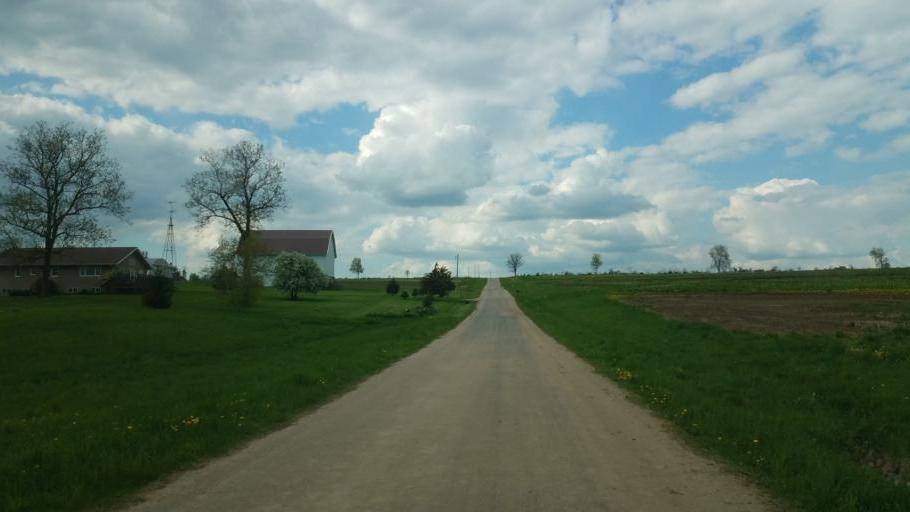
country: US
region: Wisconsin
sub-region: Vernon County
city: Hillsboro
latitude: 43.5868
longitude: -90.3317
